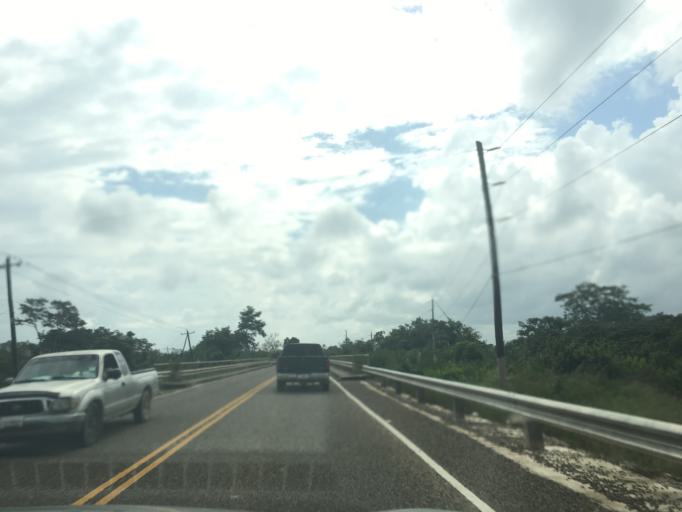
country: BZ
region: Stann Creek
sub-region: Dangriga
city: Dangriga
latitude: 17.0003
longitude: -88.3028
